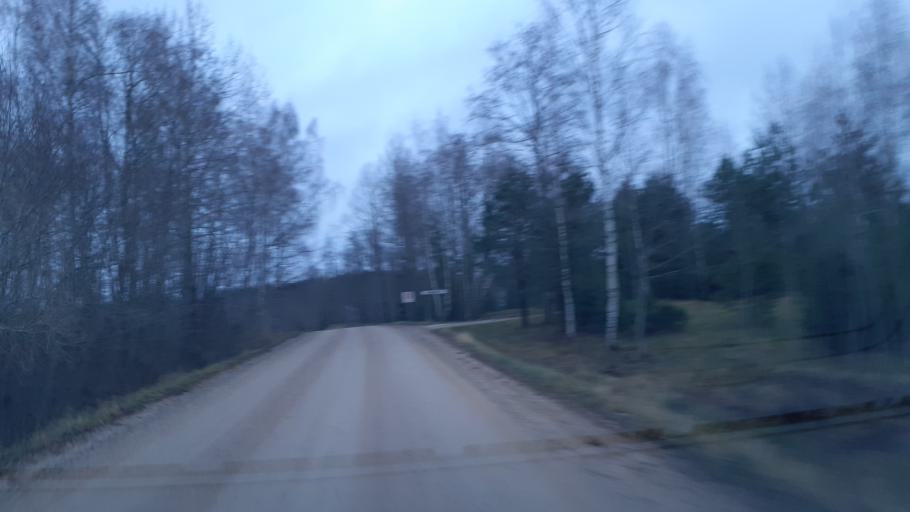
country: LV
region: Kuldigas Rajons
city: Kuldiga
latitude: 56.9857
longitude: 22.0499
